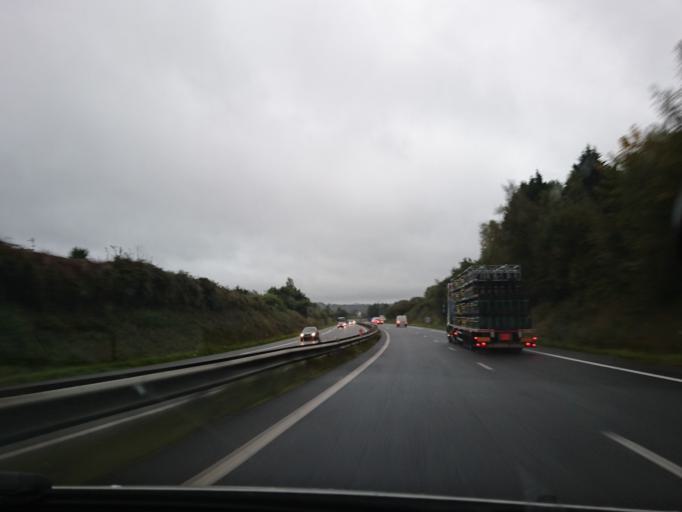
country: FR
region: Brittany
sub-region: Departement du Finistere
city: Le Relecq-Kerhuon
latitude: 48.4028
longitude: -4.4128
